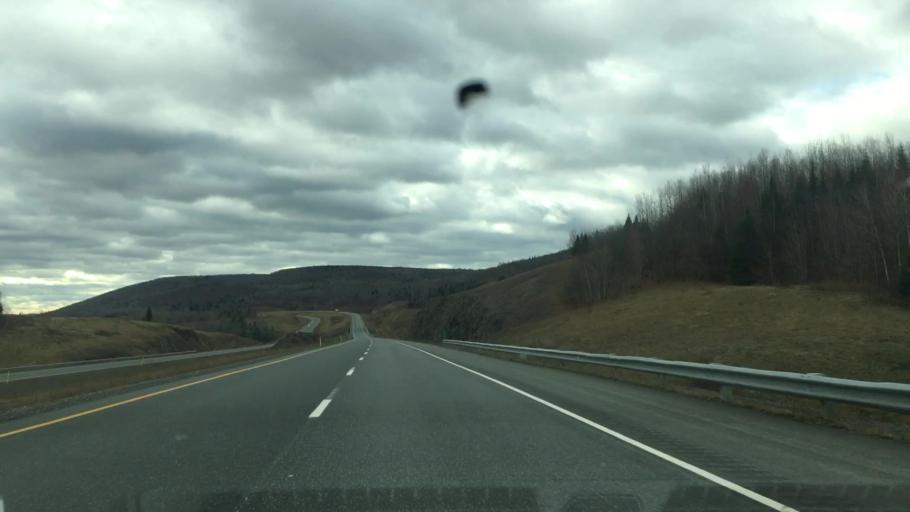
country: US
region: Maine
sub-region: Aroostook County
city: Fort Fairfield
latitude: 46.7108
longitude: -67.7365
